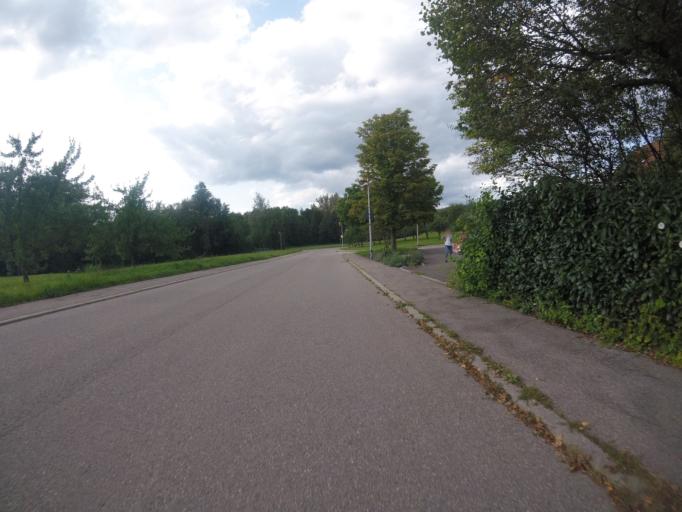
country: DE
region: Baden-Wuerttemberg
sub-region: Regierungsbezirk Stuttgart
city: Aspach
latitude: 48.9867
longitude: 9.4109
